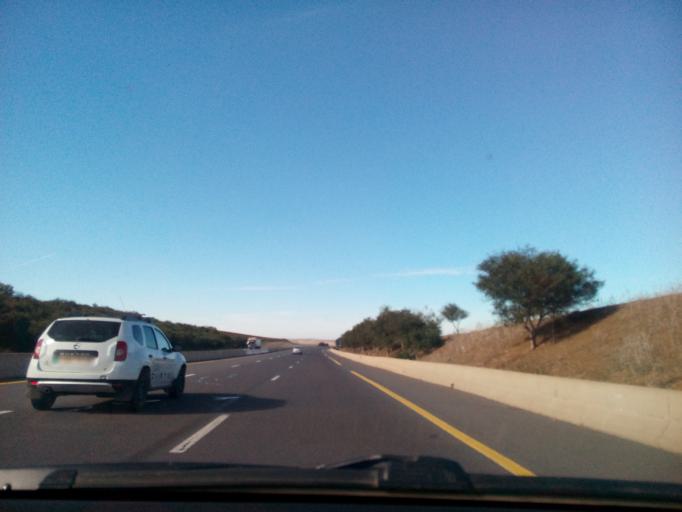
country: DZ
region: Tlemcen
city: Ouled Mimoun
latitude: 35.0312
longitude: -1.0148
